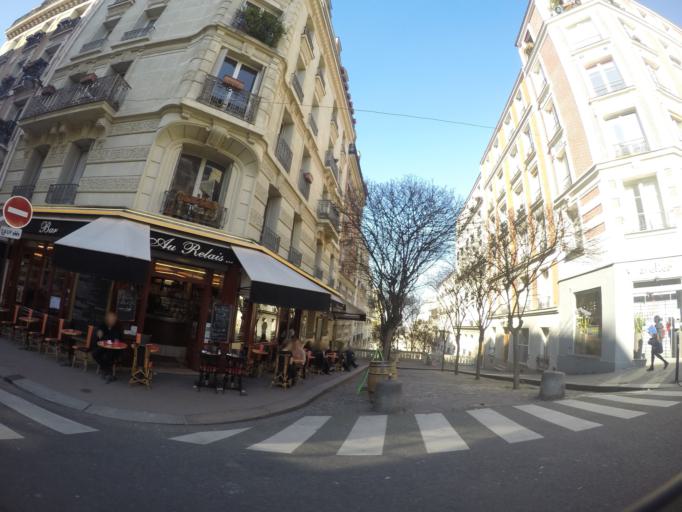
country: FR
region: Ile-de-France
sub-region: Paris
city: Saint-Ouen
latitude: 48.8892
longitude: 2.3425
